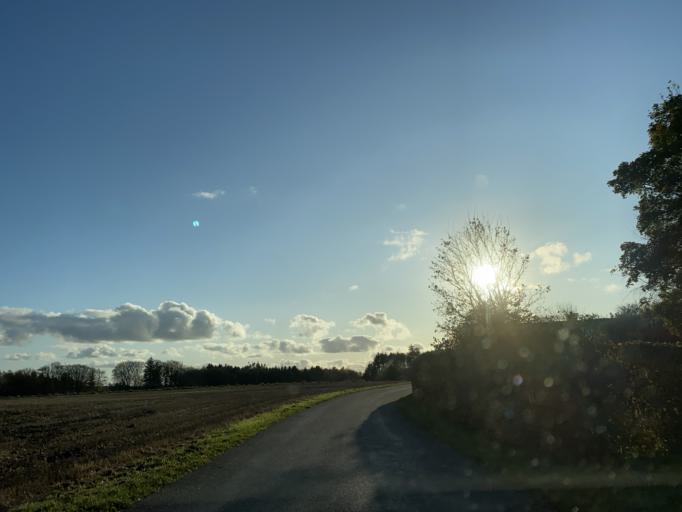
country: DK
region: Central Jutland
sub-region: Viborg Kommune
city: Bjerringbro
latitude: 56.3175
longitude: 9.6985
